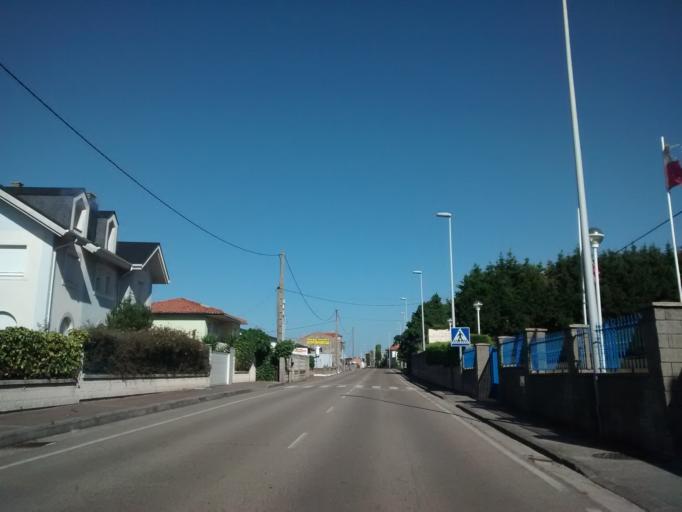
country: ES
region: Cantabria
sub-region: Provincia de Cantabria
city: Santander
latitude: 43.4654
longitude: -3.8496
